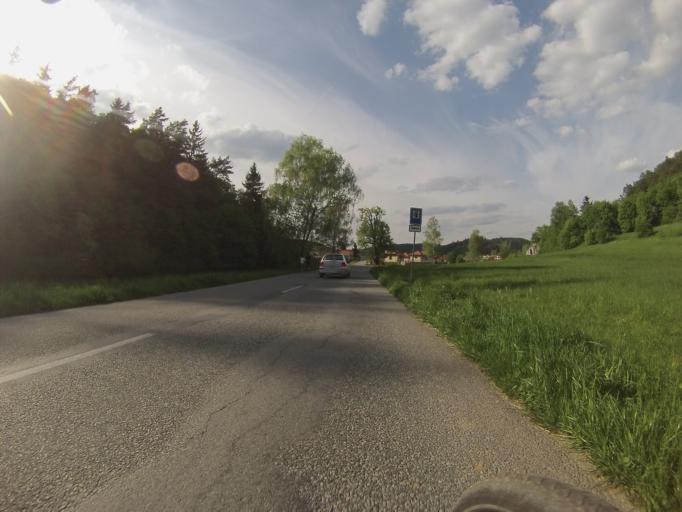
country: CZ
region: South Moravian
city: Ostrov u Macochy
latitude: 49.4089
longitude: 16.7371
